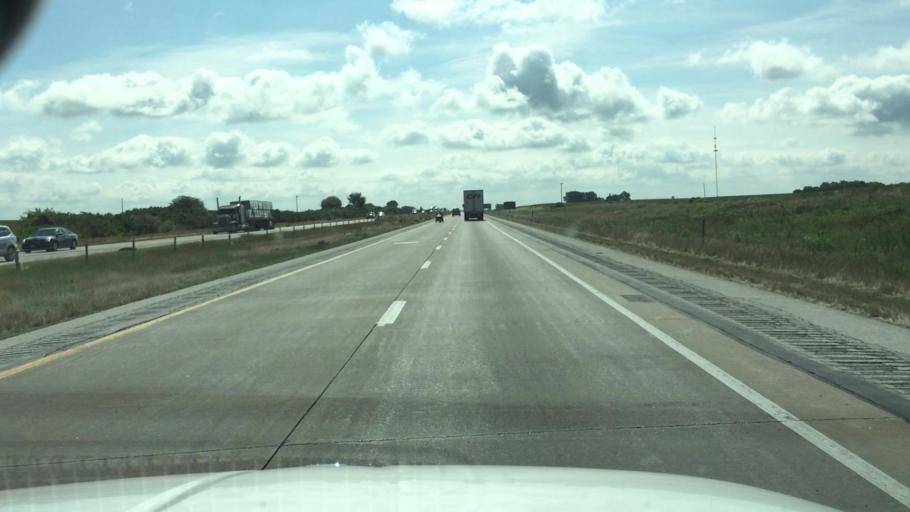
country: US
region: Iowa
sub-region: Scott County
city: Walcott
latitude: 41.6321
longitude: -90.8353
